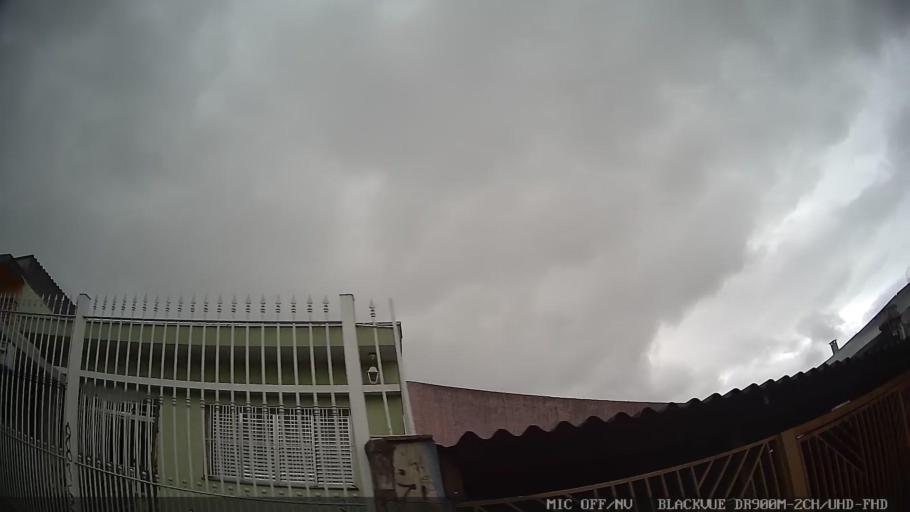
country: BR
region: Sao Paulo
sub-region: Osasco
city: Osasco
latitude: -23.4794
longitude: -46.7128
